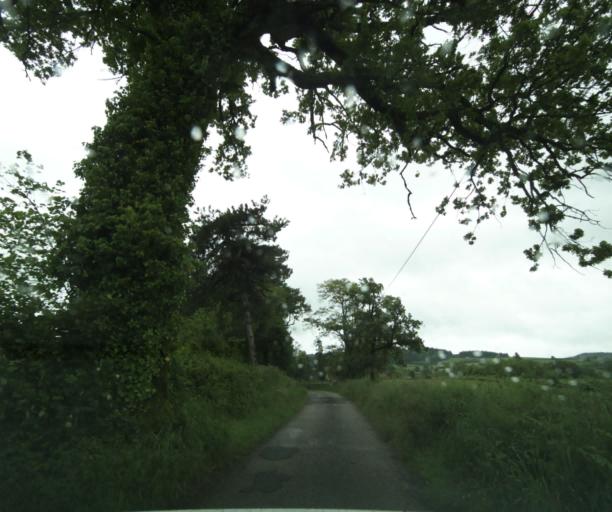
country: FR
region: Bourgogne
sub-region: Departement de Saone-et-Loire
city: Matour
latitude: 46.4633
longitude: 4.4766
